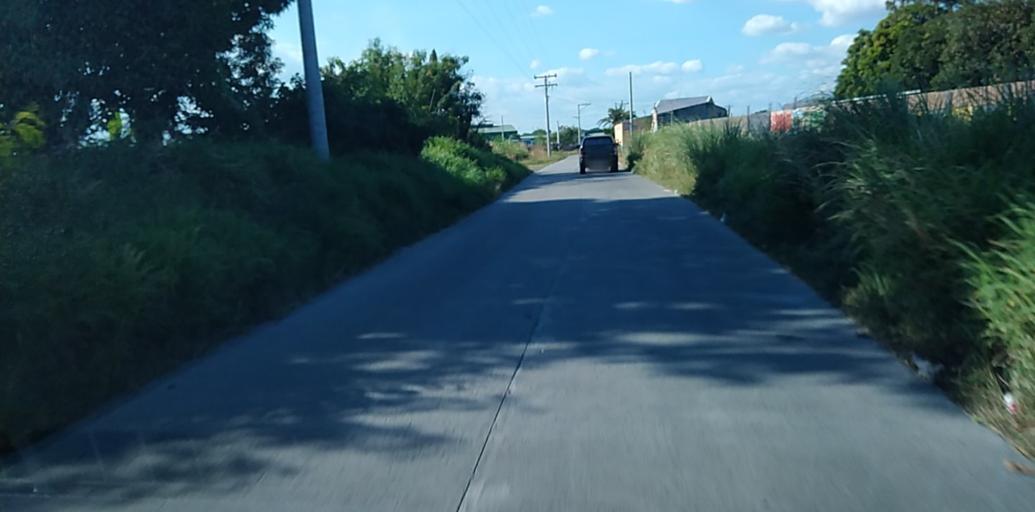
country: PH
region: Central Luzon
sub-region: Province of Pampanga
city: Acli
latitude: 15.1119
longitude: 120.6487
